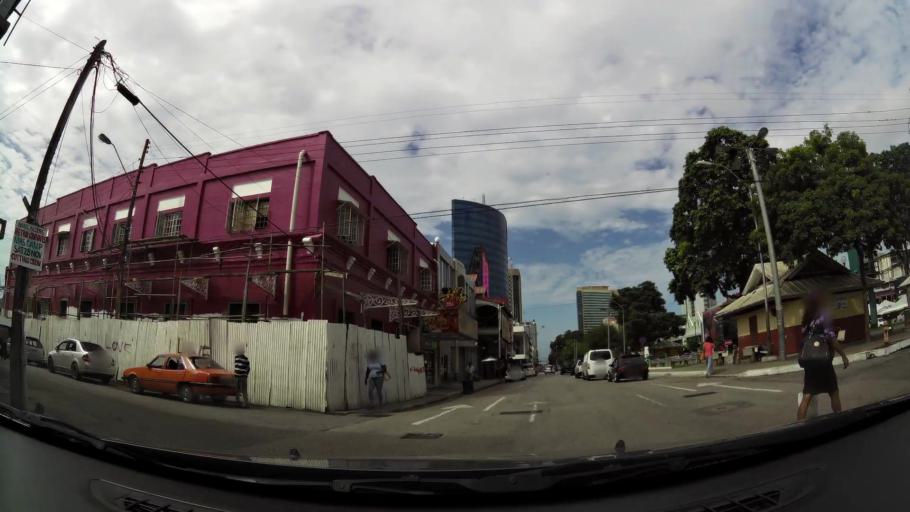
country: TT
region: San Juan/Laventille
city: Laventille
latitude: 10.6497
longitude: -61.5087
